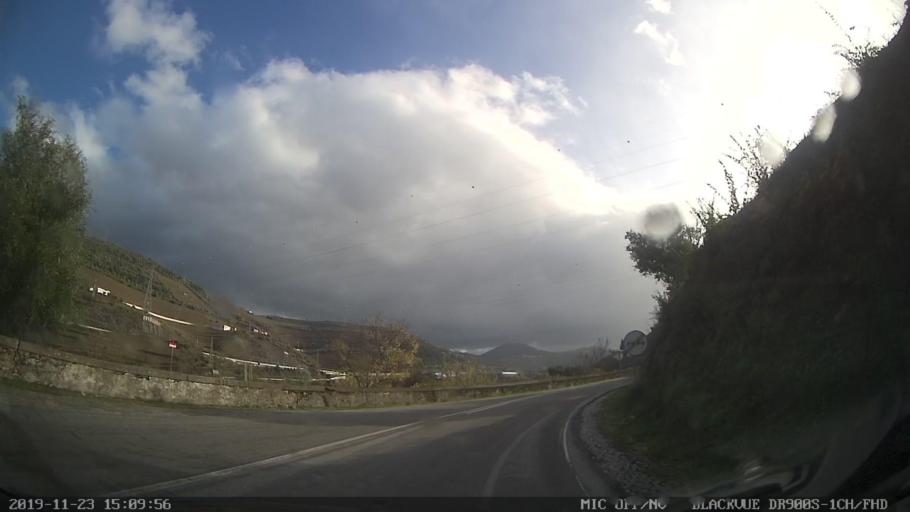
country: PT
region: Vila Real
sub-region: Peso da Regua
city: Peso da Regua
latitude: 41.1446
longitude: -7.7792
